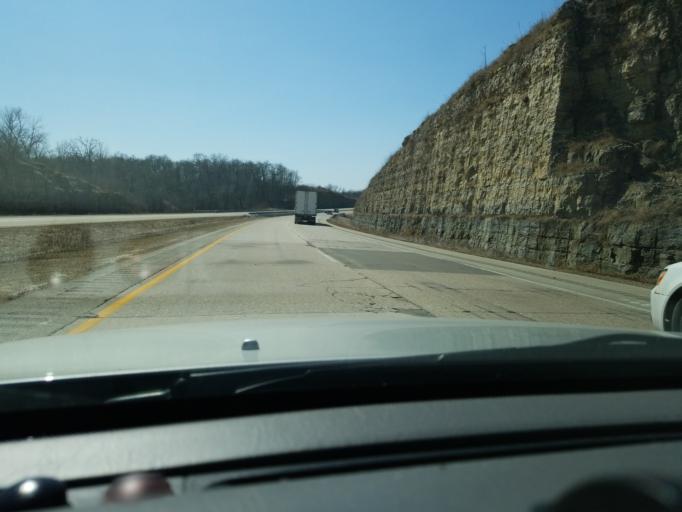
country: US
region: Wisconsin
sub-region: Iowa County
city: Barneveld
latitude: 42.9986
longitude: -89.9826
